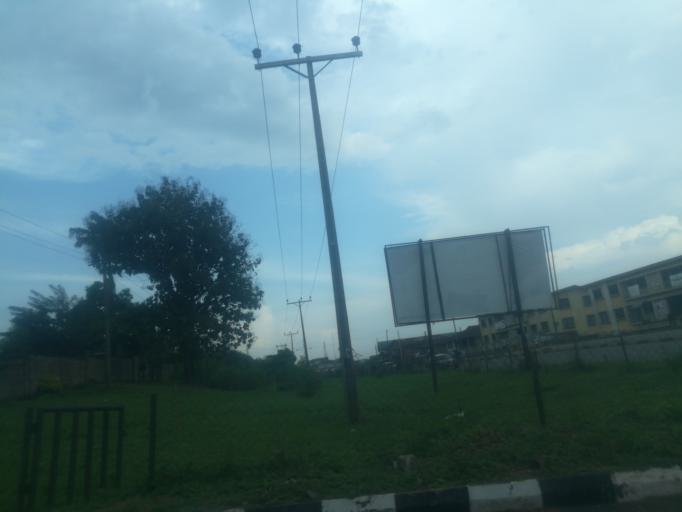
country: NG
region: Oyo
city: Ibadan
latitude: 7.4270
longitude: 3.8888
